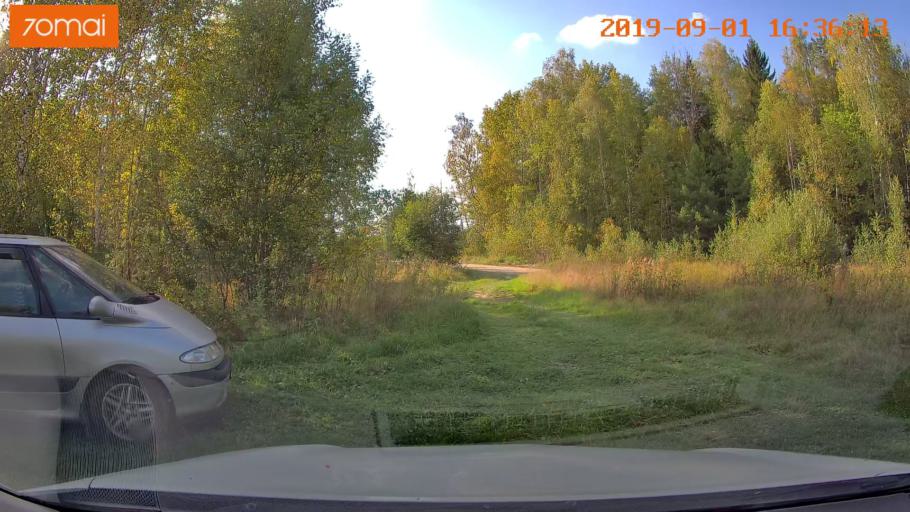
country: RU
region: Kaluga
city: Maloyaroslavets
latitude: 54.9477
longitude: 36.4766
